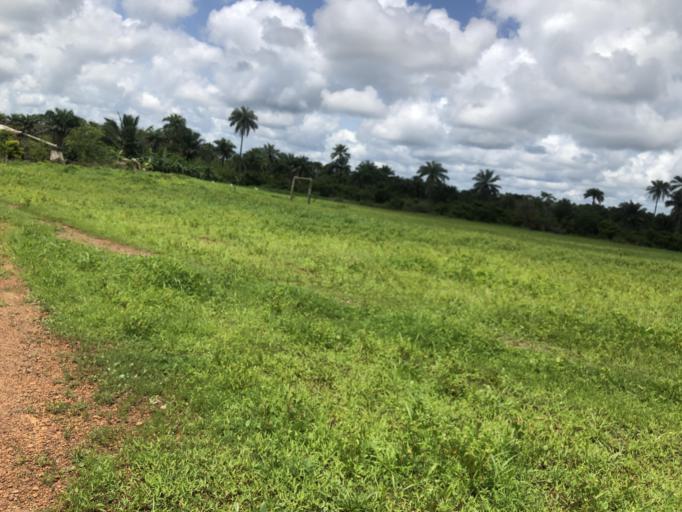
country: SL
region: Northern Province
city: Port Loko
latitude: 8.7176
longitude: -12.8476
